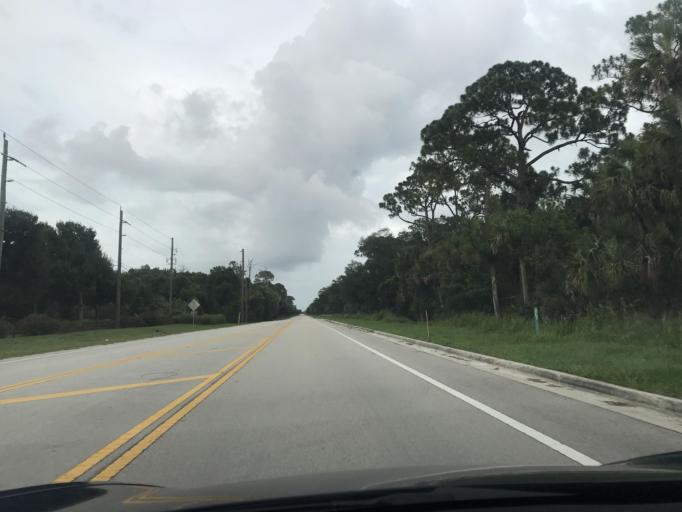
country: US
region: Florida
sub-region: Indian River County
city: West Vero Corridor
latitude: 27.6169
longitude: -80.4623
